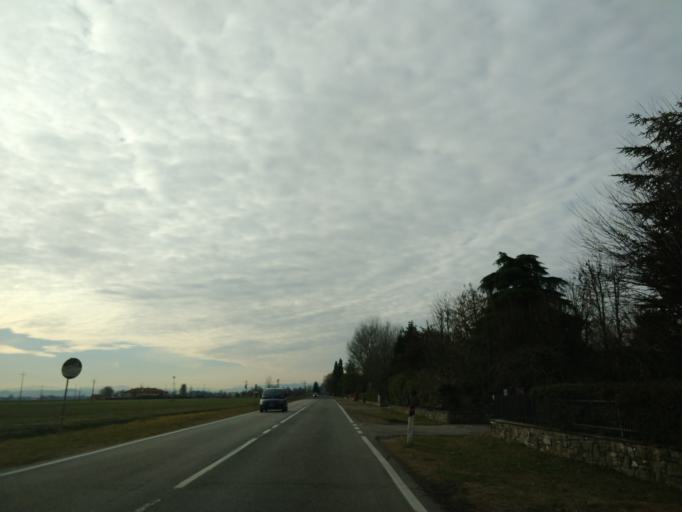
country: IT
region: Emilia-Romagna
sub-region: Provincia di Bologna
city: Argelato
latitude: 44.6323
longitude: 11.3434
